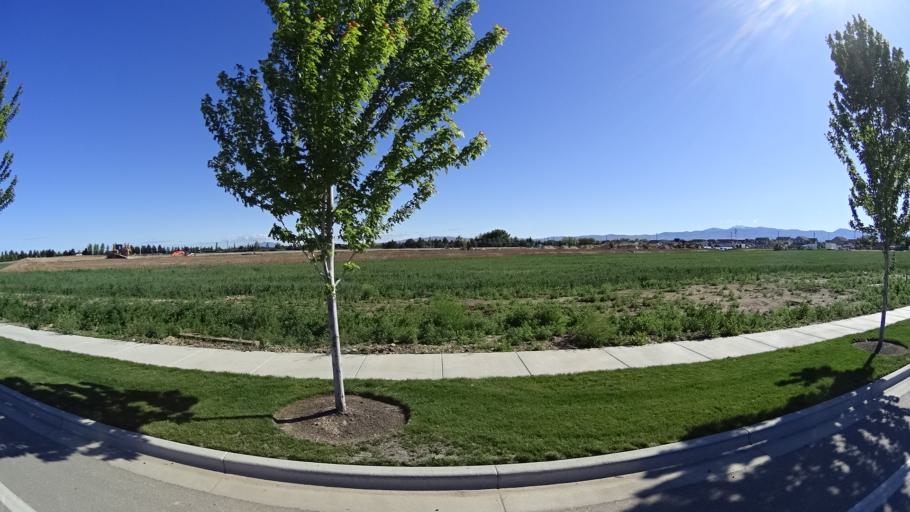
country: US
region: Idaho
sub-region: Ada County
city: Star
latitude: 43.6594
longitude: -116.4378
